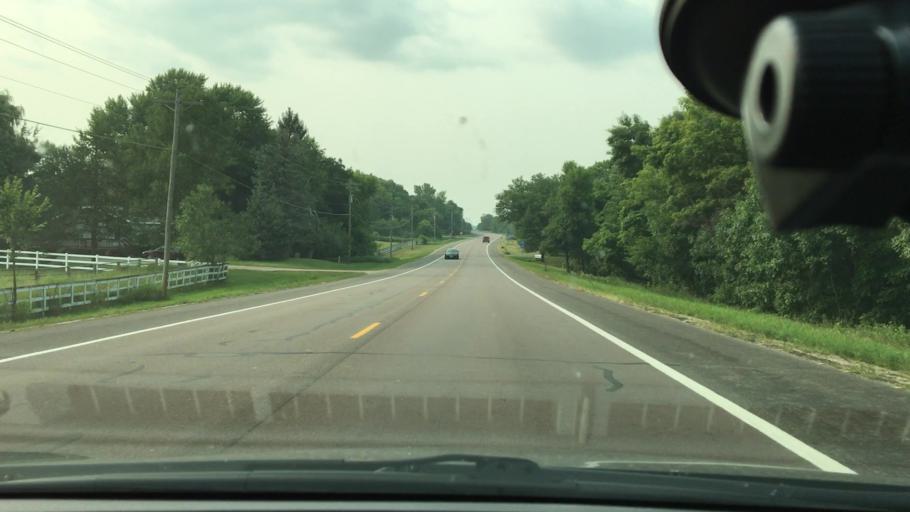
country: US
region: Minnesota
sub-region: Hennepin County
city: Dayton
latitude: 45.2496
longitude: -93.5351
